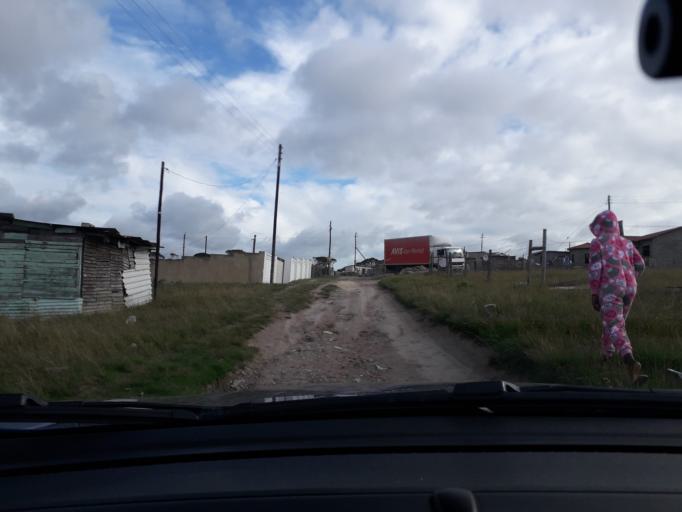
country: ZA
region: Eastern Cape
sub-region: Buffalo City Metropolitan Municipality
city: East London
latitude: -32.8515
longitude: 27.9857
